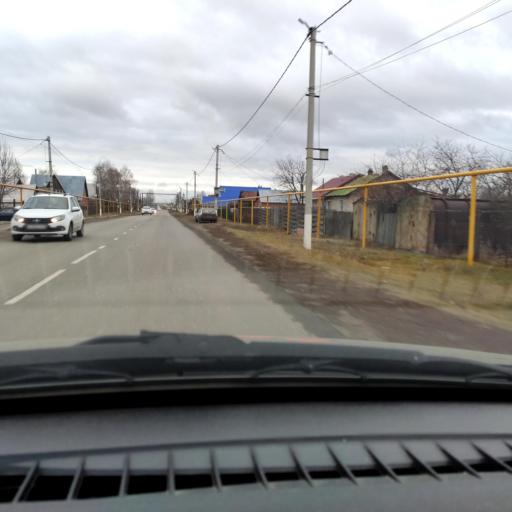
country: RU
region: Samara
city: Podstepki
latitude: 53.5162
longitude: 49.1238
